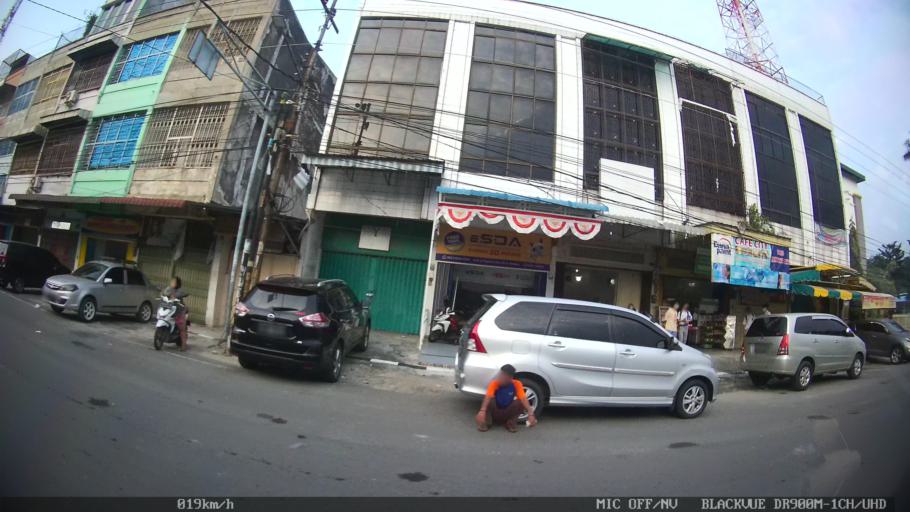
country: ID
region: North Sumatra
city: Medan
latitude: 3.5926
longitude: 98.6891
